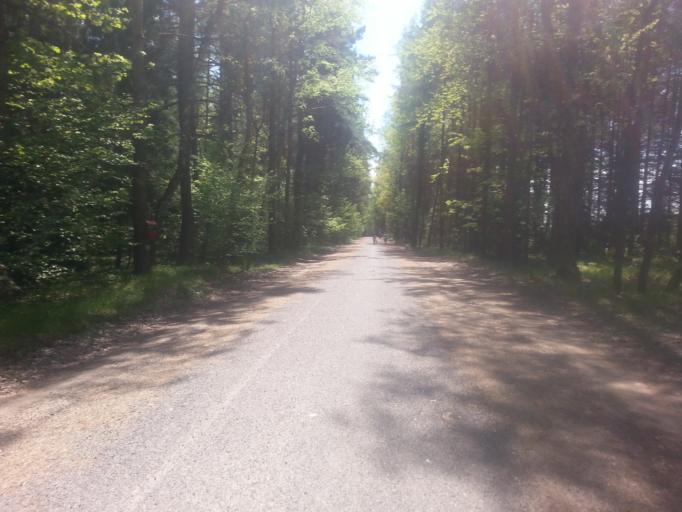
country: BY
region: Minsk
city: Narach
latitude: 54.9228
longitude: 26.6933
